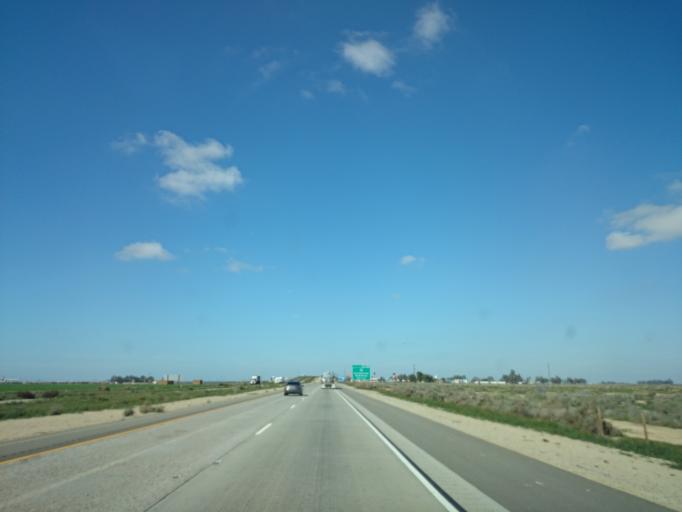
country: US
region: California
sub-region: Kern County
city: Buttonwillow
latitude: 35.3925
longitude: -119.3884
